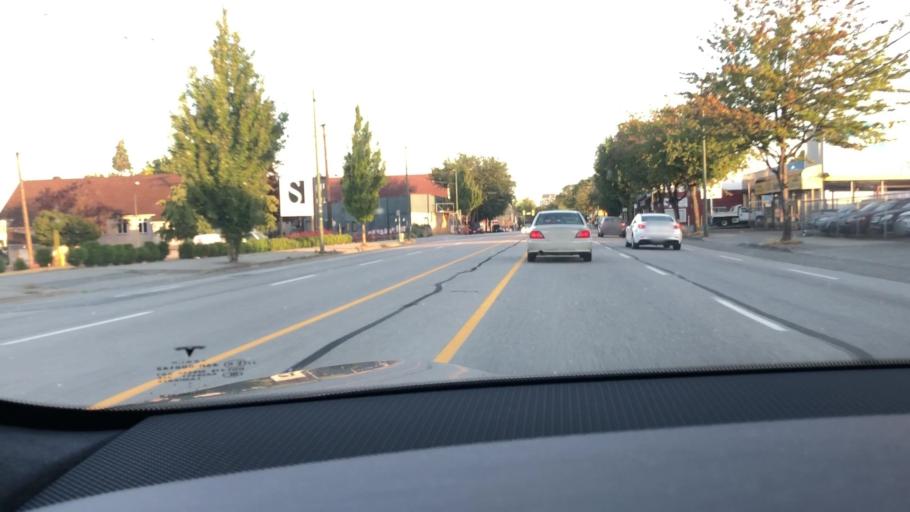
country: CA
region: British Columbia
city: Vancouver
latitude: 49.2552
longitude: -123.0865
